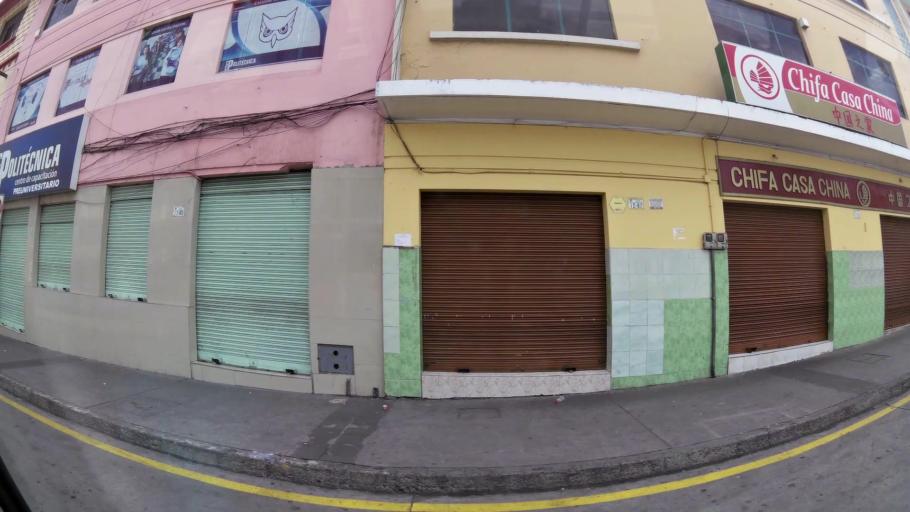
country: EC
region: Tungurahua
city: Ambato
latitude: -1.2416
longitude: -78.6248
